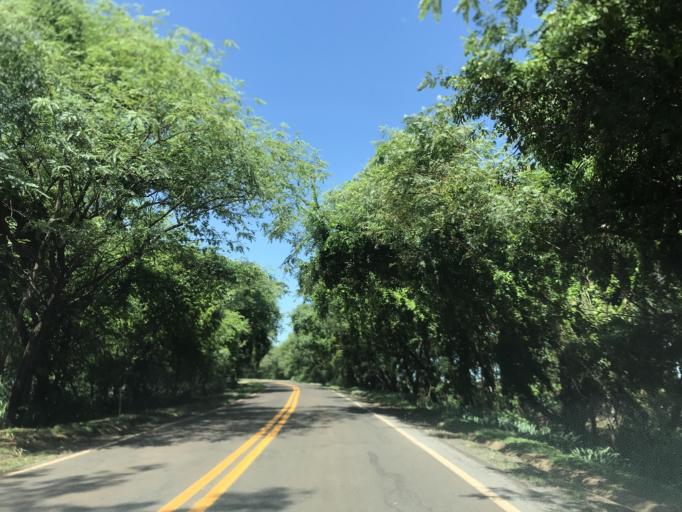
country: BR
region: Parana
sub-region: Terra Rica
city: Terra Rica
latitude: -22.7760
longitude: -52.6548
